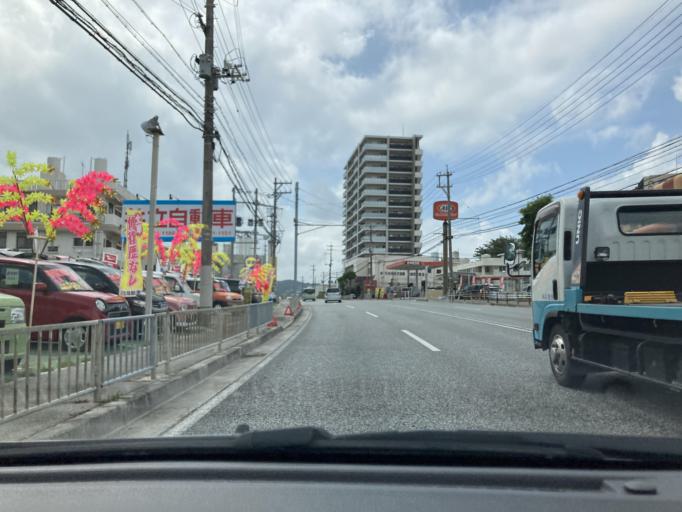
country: JP
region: Okinawa
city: Okinawa
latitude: 26.3121
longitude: 127.8169
